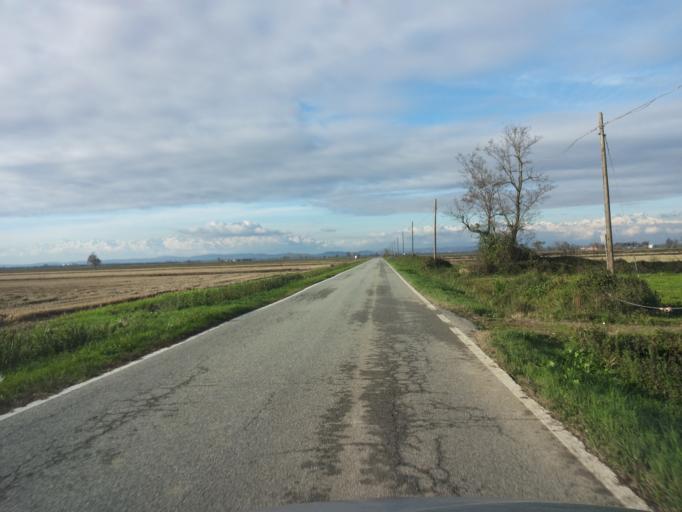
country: IT
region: Piedmont
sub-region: Provincia di Vercelli
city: Crova
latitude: 45.3008
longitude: 8.2144
